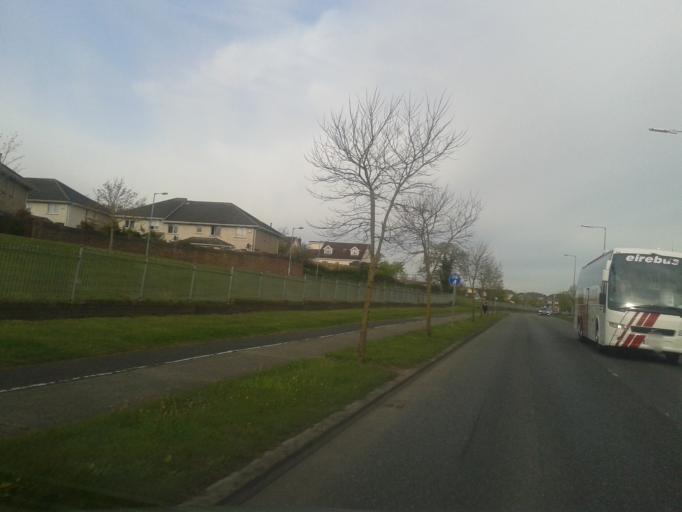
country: IE
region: Leinster
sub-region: Fingal County
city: Swords
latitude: 53.4683
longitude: -6.2252
